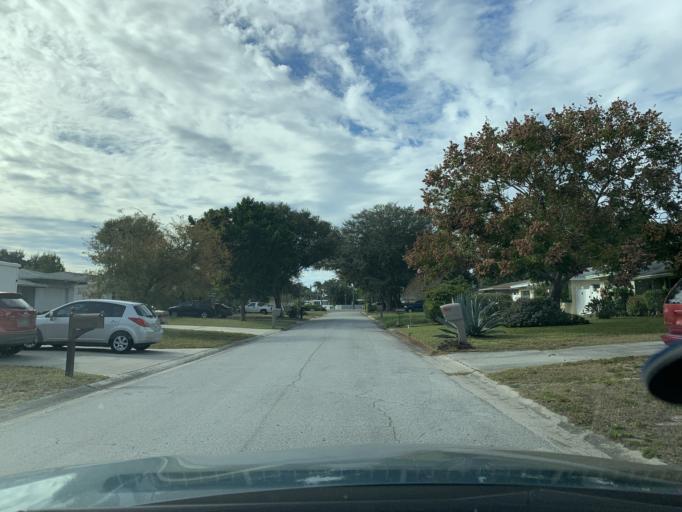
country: US
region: Florida
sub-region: Pinellas County
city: Kenneth City
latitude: 27.8096
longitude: -82.7356
